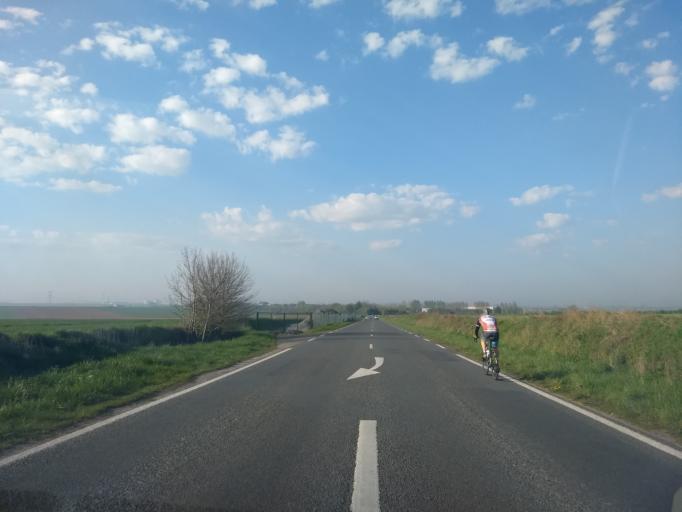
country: FR
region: Nord-Pas-de-Calais
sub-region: Departement du Pas-de-Calais
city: Agny
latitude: 50.2483
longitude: 2.7702
